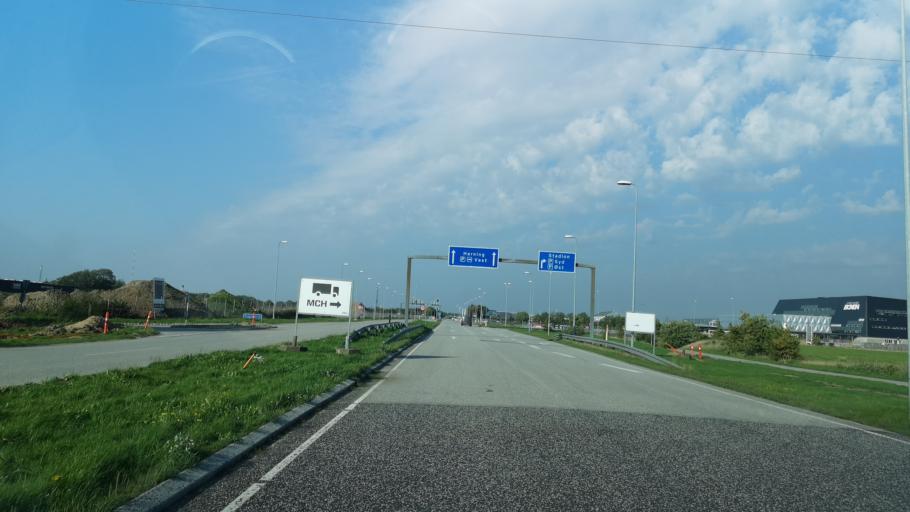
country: DK
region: Central Jutland
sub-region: Herning Kommune
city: Herning
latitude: 56.1152
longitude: 8.9455
